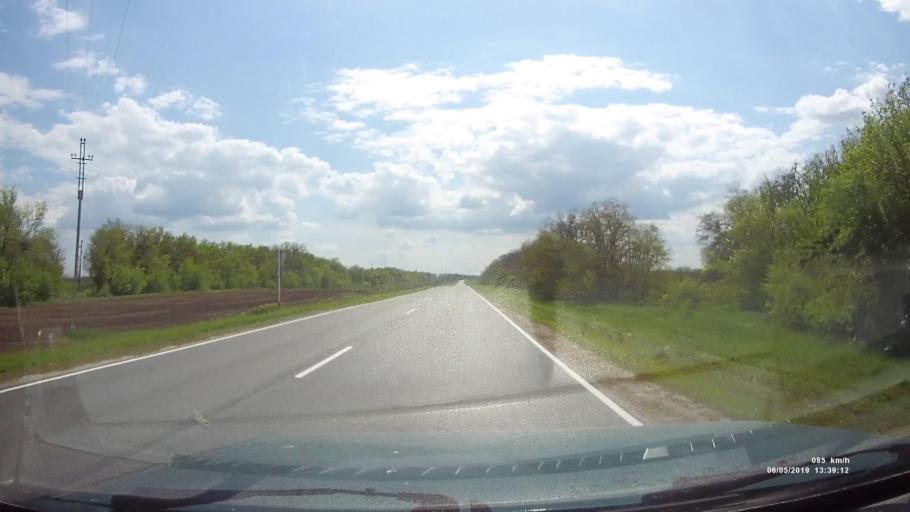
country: RU
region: Rostov
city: Ust'-Donetskiy
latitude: 47.6788
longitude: 40.7048
